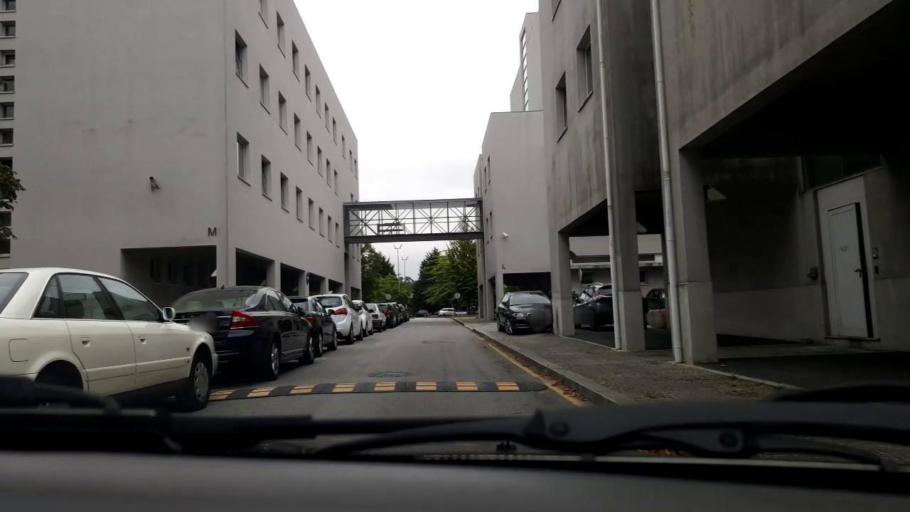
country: PT
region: Porto
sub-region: Maia
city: Pedroucos
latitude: 41.1785
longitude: -8.5951
